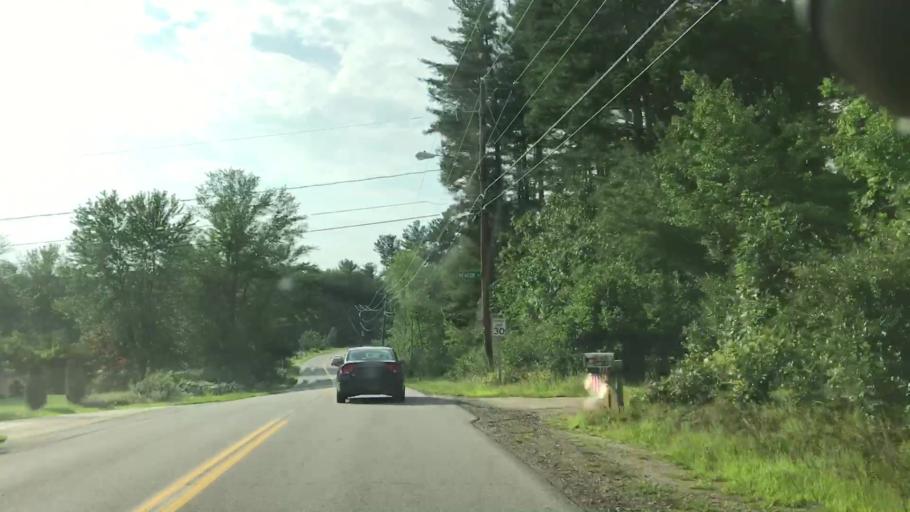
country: US
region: New Hampshire
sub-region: Hillsborough County
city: Hollis
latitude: 42.8122
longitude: -71.5646
